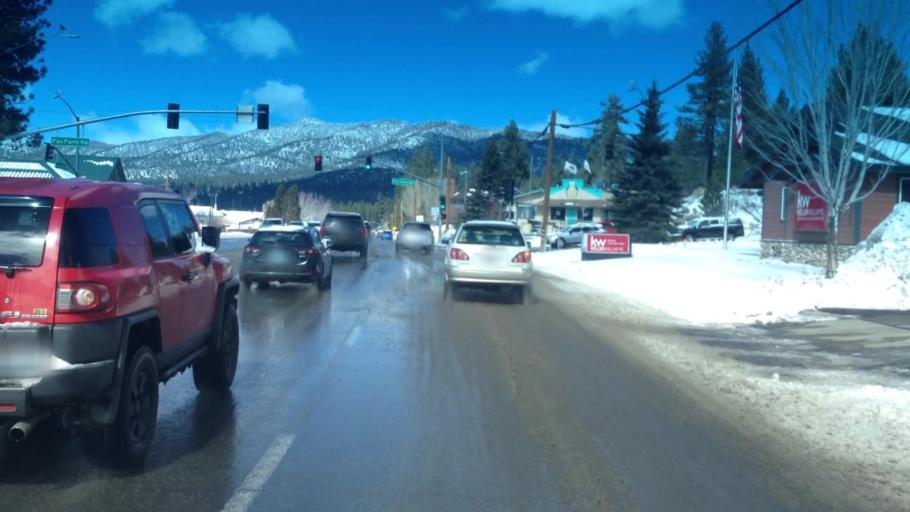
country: US
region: California
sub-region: San Bernardino County
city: Big Bear Lake
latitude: 34.2482
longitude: -116.8827
